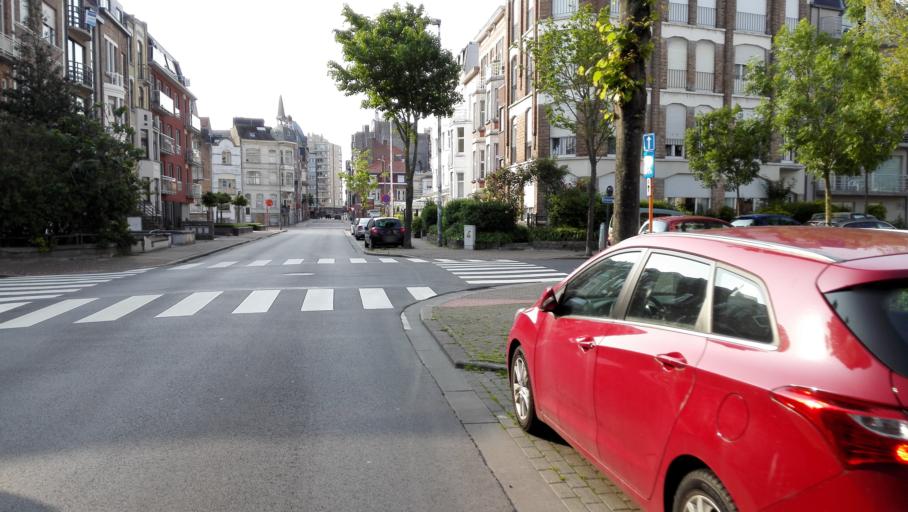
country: BE
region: Flanders
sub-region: Provincie West-Vlaanderen
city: Blankenberge
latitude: 51.3144
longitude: 3.1339
